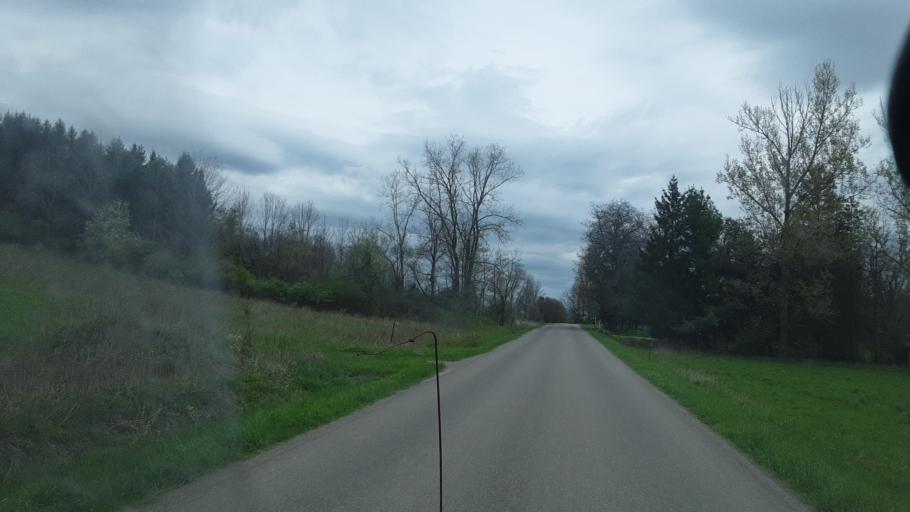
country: US
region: New York
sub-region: Steuben County
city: Addison
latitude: 42.0970
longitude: -77.2714
